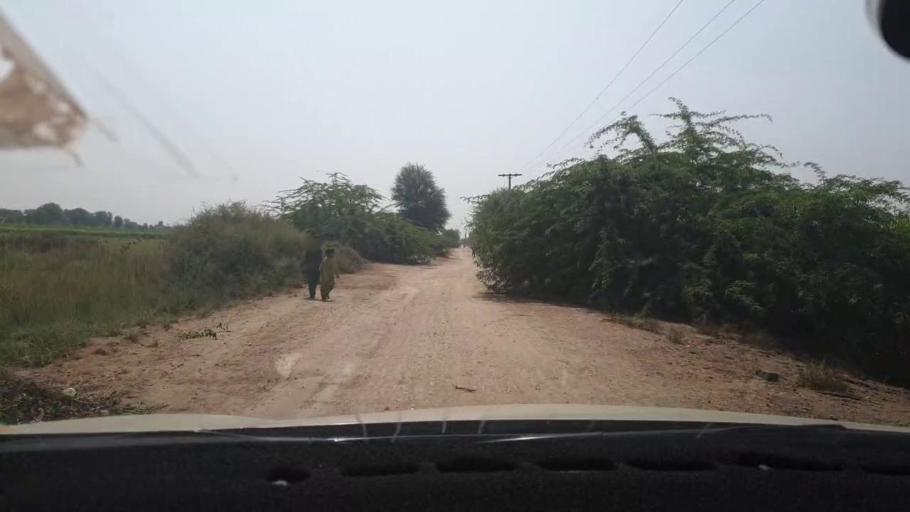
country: PK
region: Sindh
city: Tando Mittha Khan
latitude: 25.9433
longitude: 69.2247
